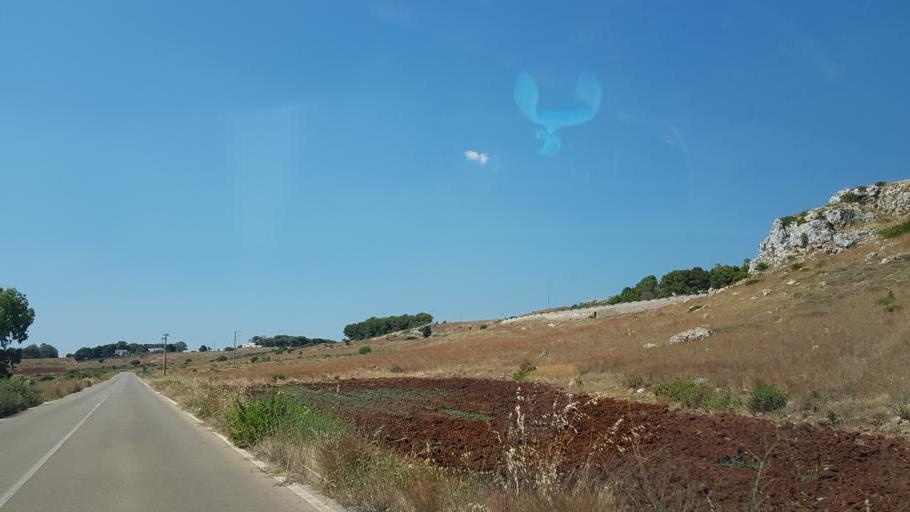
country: IT
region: Apulia
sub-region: Provincia di Lecce
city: Nardo
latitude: 40.1723
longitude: 17.9470
